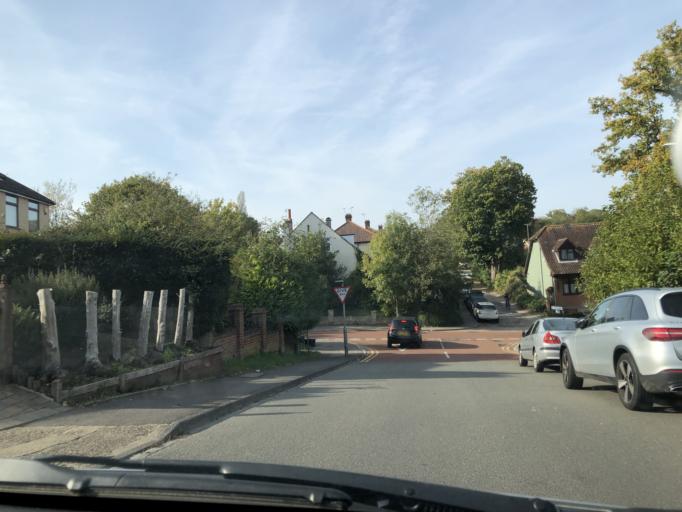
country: GB
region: England
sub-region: Greater London
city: Bexley
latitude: 51.4269
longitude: 0.1680
